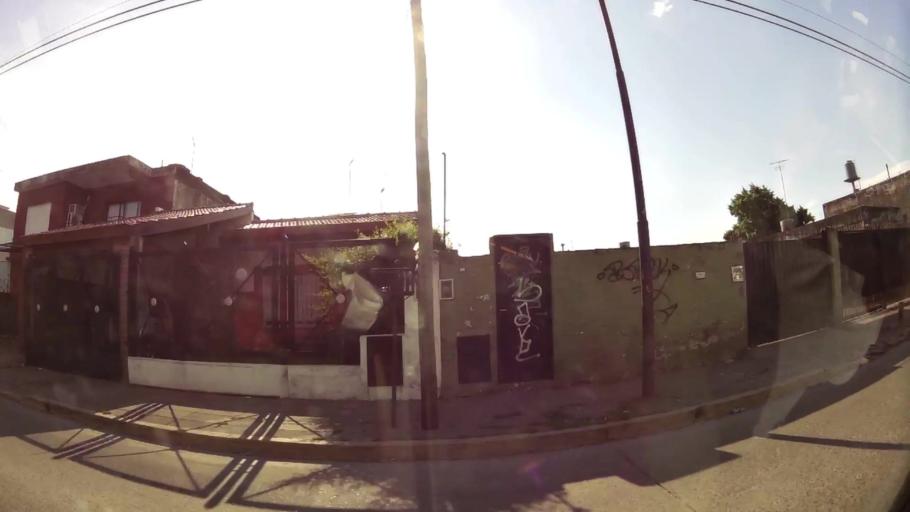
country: AR
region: Buenos Aires
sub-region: Partido de Merlo
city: Merlo
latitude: -34.6642
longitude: -58.7143
